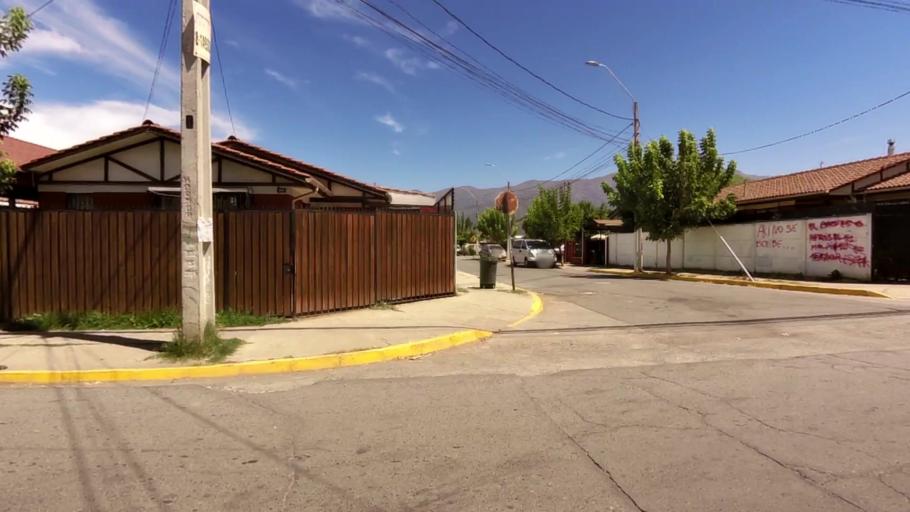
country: CL
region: O'Higgins
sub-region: Provincia de Cachapoal
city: Graneros
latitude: -34.0641
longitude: -70.7224
